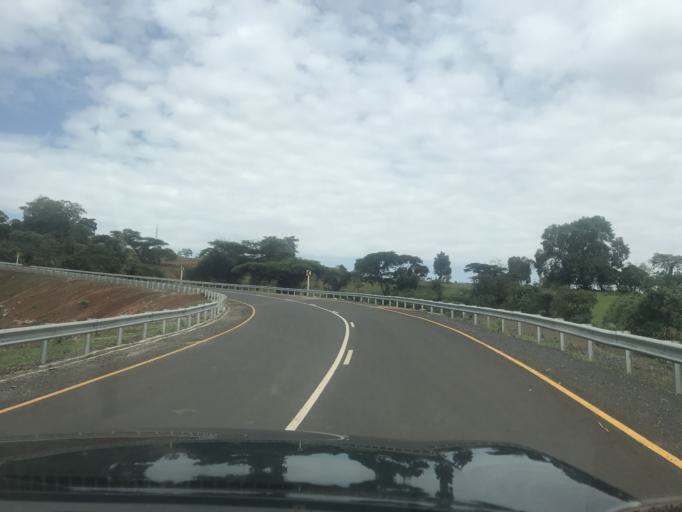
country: ET
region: Oromiya
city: Shambu
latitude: 9.8721
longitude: 36.6935
